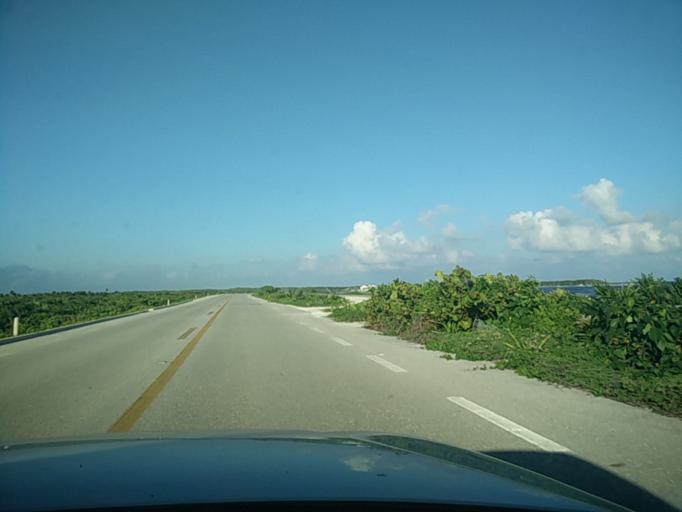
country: MX
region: Quintana Roo
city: San Miguel de Cozumel
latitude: 20.3426
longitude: -86.9098
